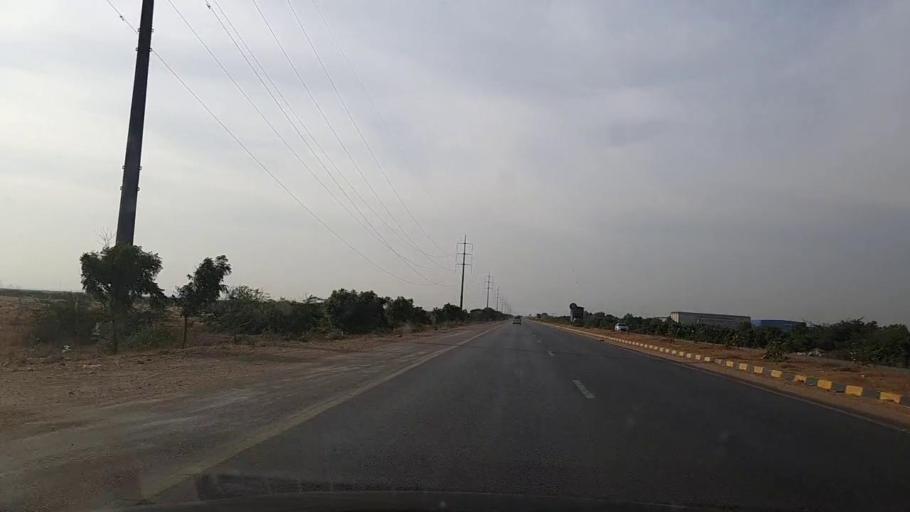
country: PK
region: Sindh
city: Gharo
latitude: 24.8256
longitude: 67.4741
